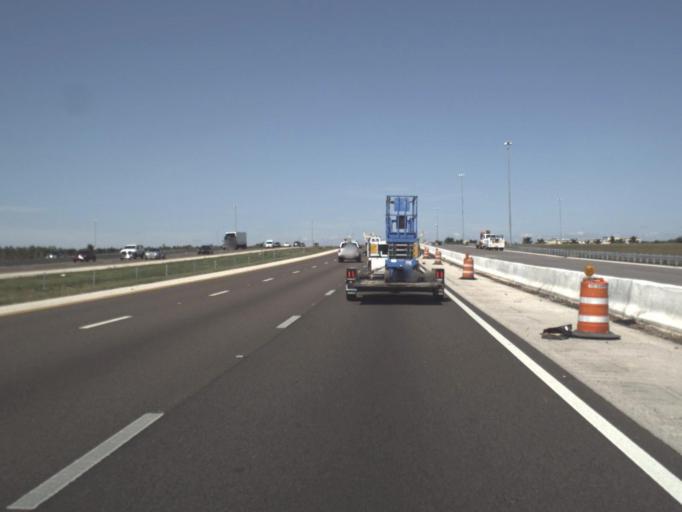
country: US
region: Florida
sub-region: Lee County
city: Three Oaks
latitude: 26.4881
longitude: -81.7942
